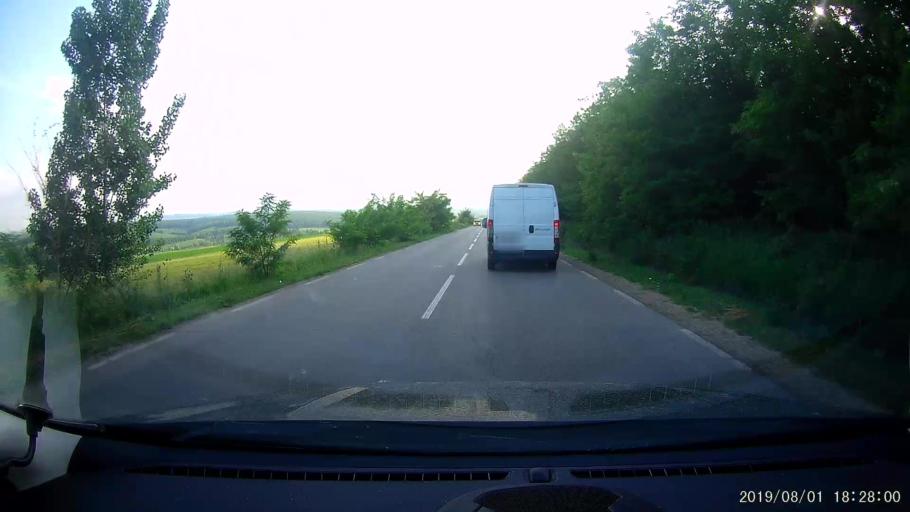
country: BG
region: Shumen
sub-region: Obshtina Venets
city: Venets
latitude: 43.5796
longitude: 26.9726
